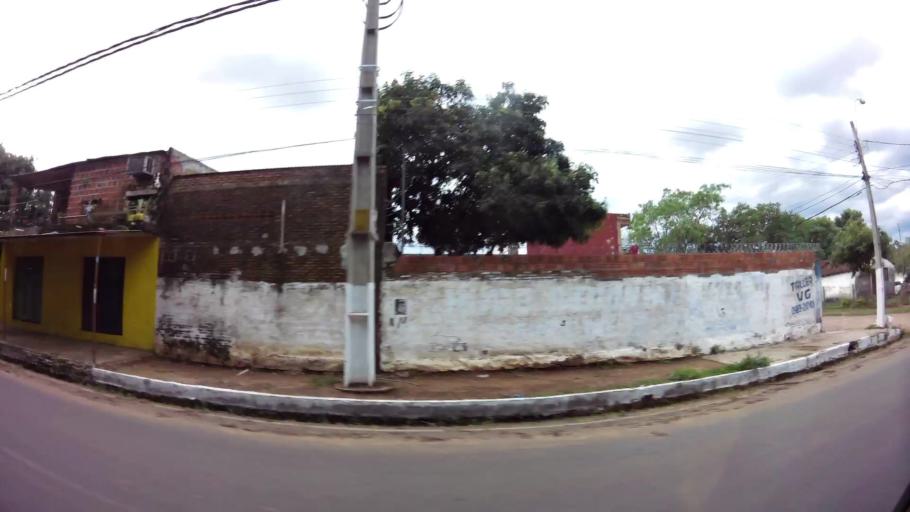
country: PY
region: Central
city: San Lorenzo
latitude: -25.2810
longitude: -57.4884
